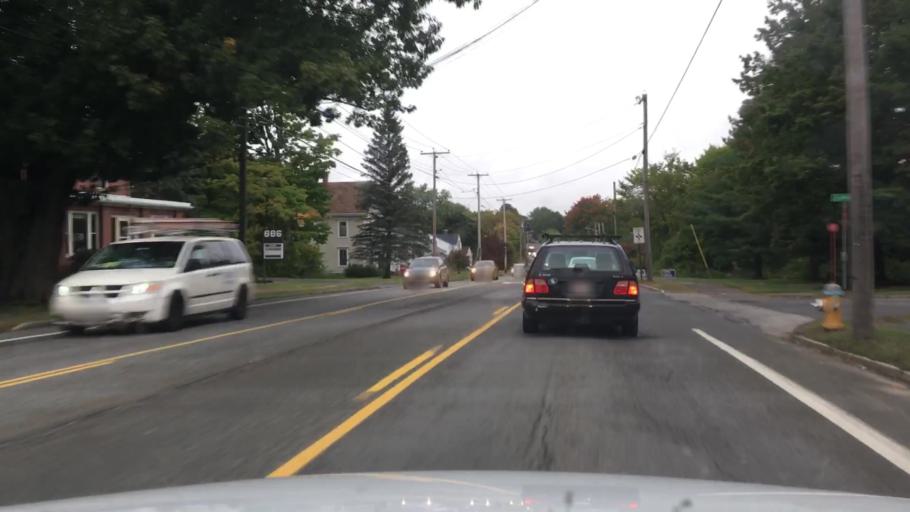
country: US
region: Maine
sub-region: Cumberland County
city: South Portland Gardens
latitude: 43.6704
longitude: -70.3061
